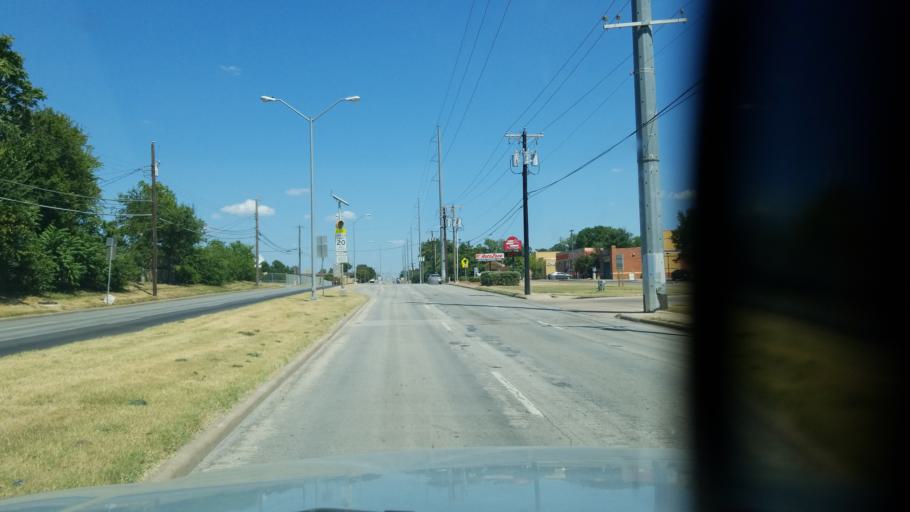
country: US
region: Texas
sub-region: Dallas County
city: Cockrell Hill
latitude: 32.7204
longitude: -96.8830
